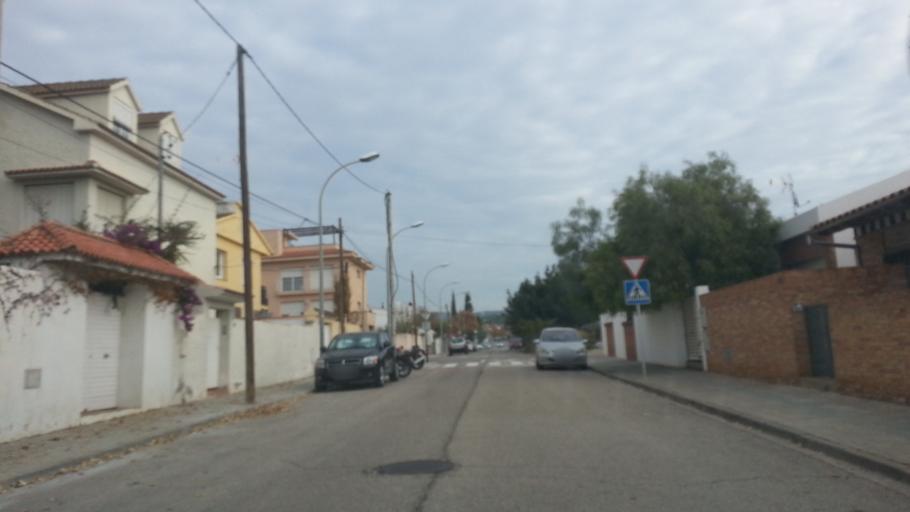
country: ES
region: Catalonia
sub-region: Provincia de Barcelona
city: Sant Pere de Ribes
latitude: 41.2561
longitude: 1.7767
